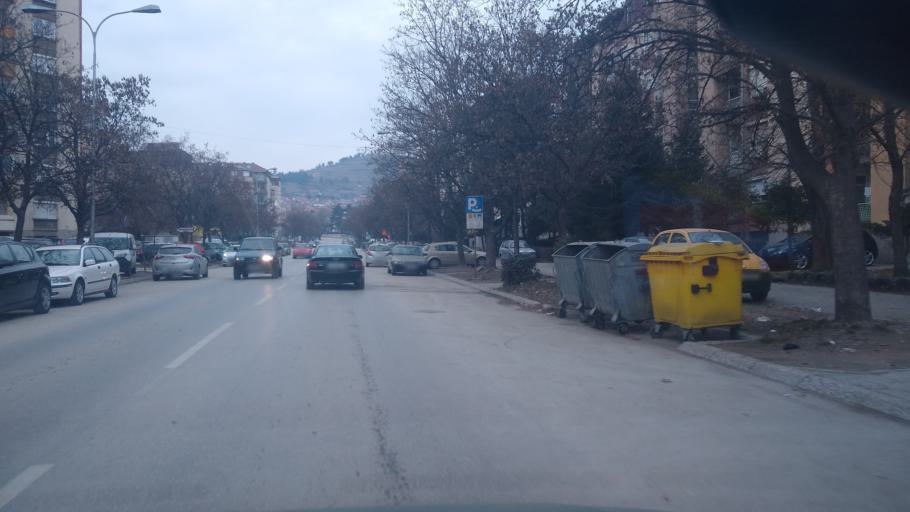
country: MK
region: Bitola
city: Bitola
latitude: 41.0341
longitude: 21.3411
